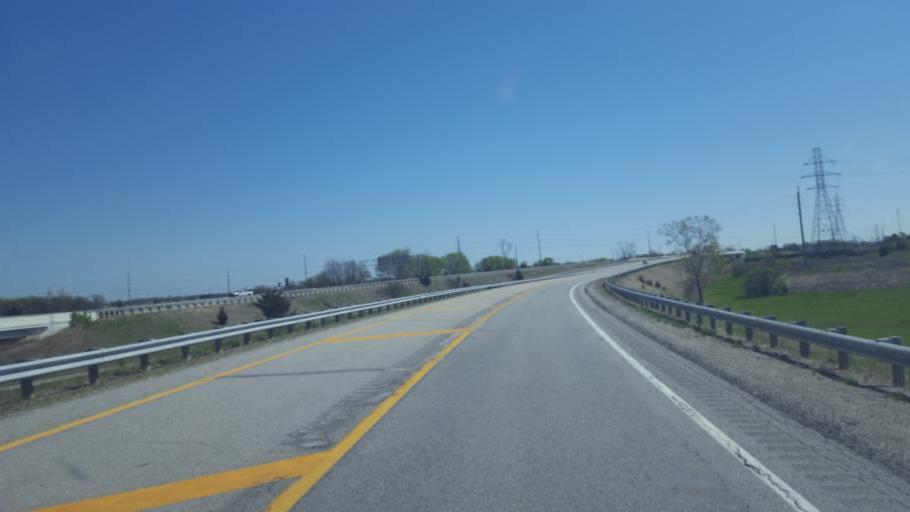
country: US
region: Ohio
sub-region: Sandusky County
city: Stony Prairie
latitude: 41.3676
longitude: -83.1587
